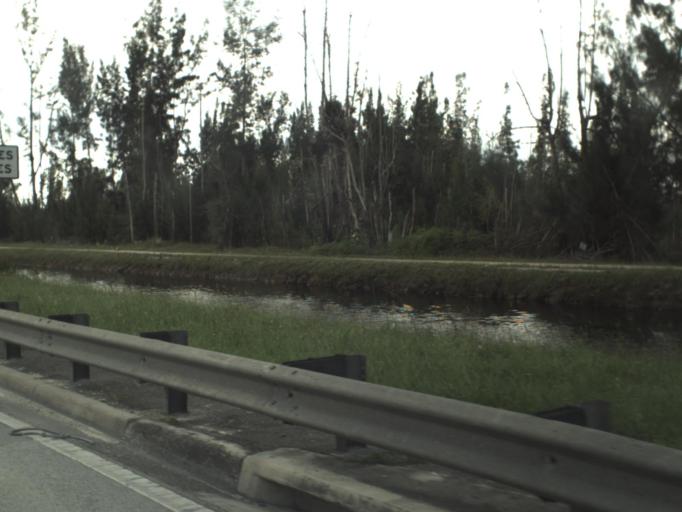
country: US
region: Florida
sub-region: Miami-Dade County
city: Tamiami
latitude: 25.7611
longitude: -80.4223
